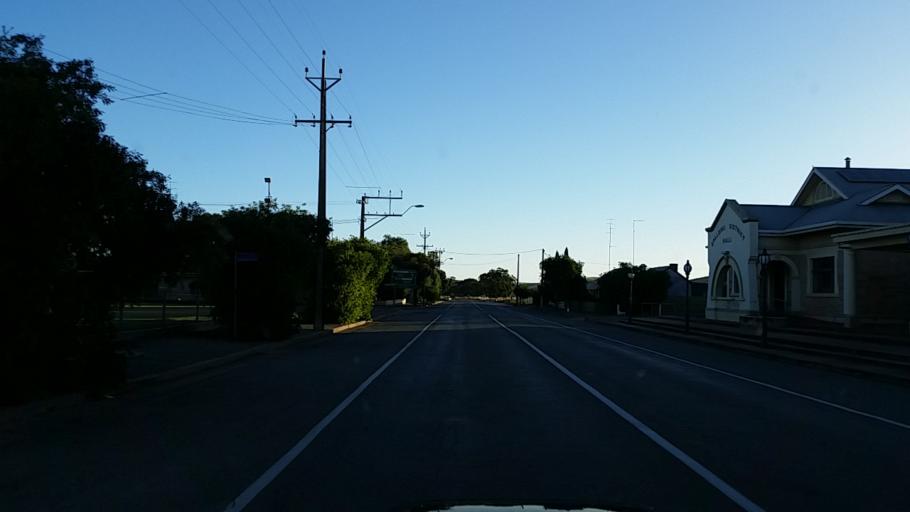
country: AU
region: South Australia
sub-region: Northern Areas
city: Jamestown
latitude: -33.4996
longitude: 138.6073
